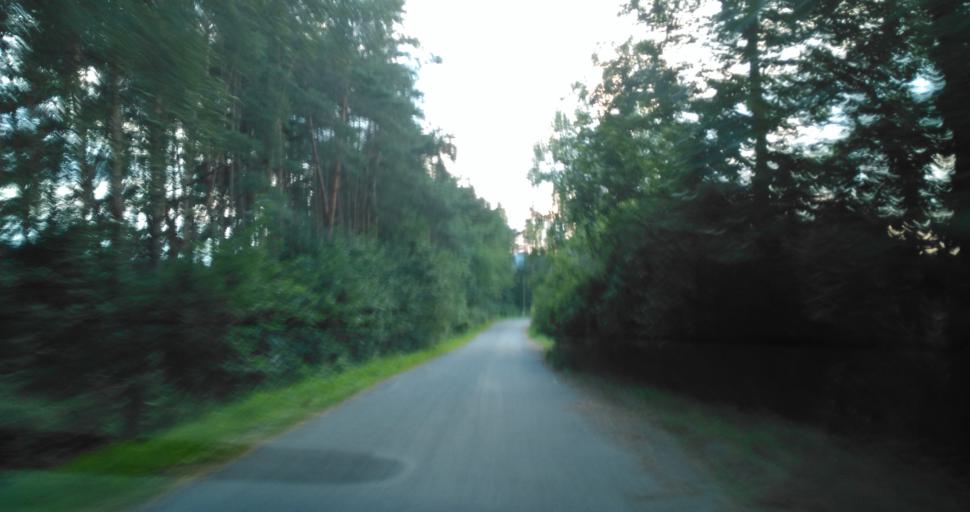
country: CZ
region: Plzensky
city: Zbiroh
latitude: 49.8520
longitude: 13.7444
